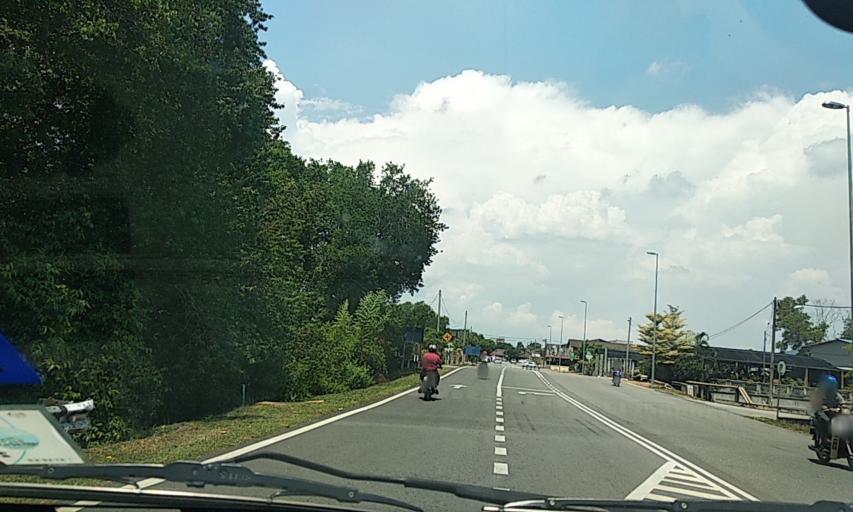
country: MY
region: Kedah
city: Sungai Petani
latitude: 5.6375
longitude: 100.4823
